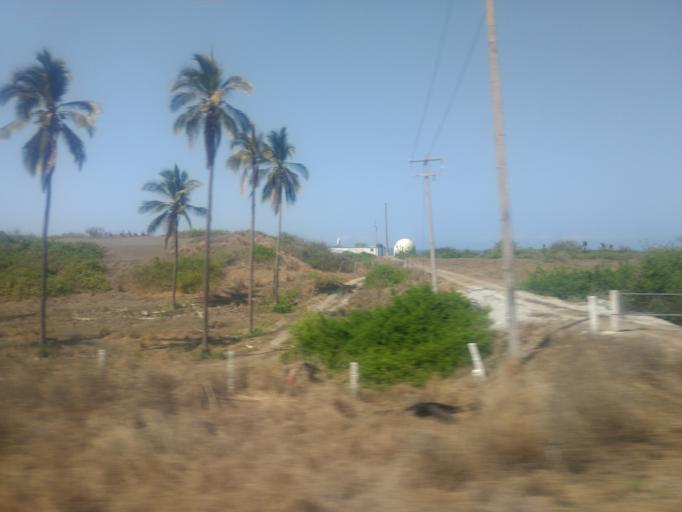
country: MX
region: Colima
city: Armeria
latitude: 18.9374
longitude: -104.0991
